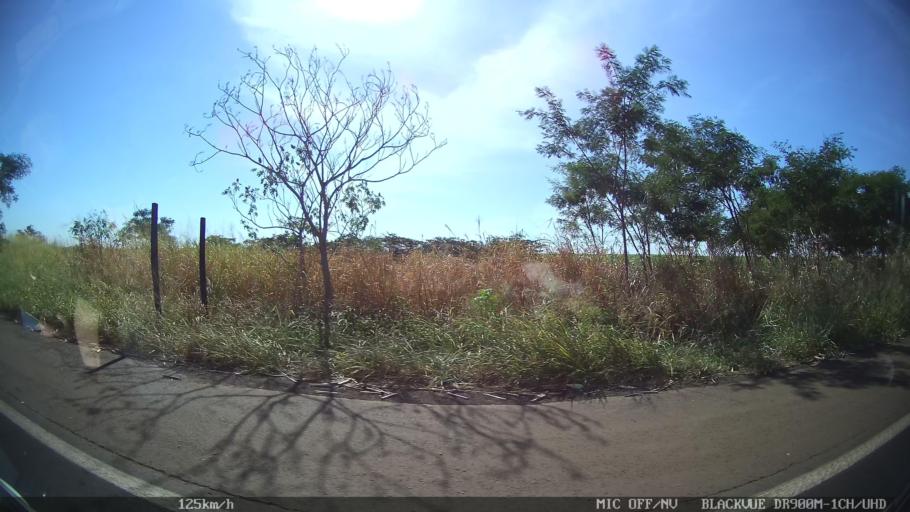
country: BR
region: Sao Paulo
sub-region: Olimpia
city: Olimpia
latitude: -20.6262
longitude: -48.7890
